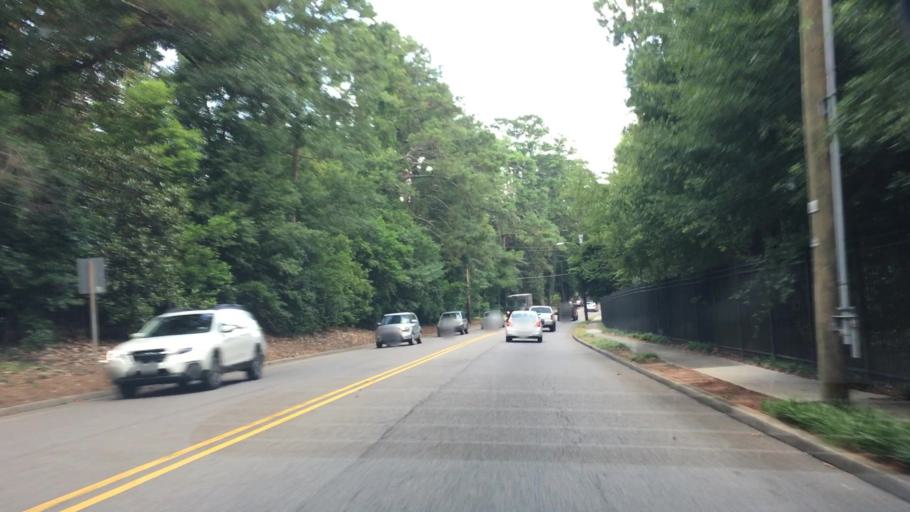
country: US
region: South Carolina
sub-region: Aiken County
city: Aiken
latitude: 33.5476
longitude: -81.7213
